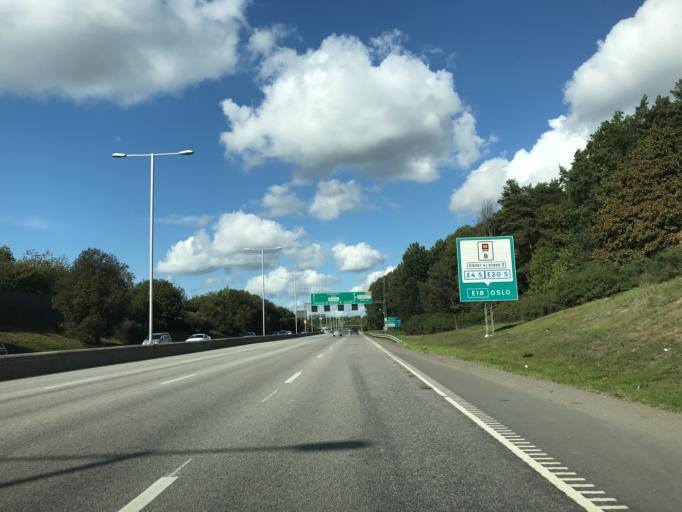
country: SE
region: Stockholm
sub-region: Solna Kommun
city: Solna
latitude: 59.3829
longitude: 18.0078
